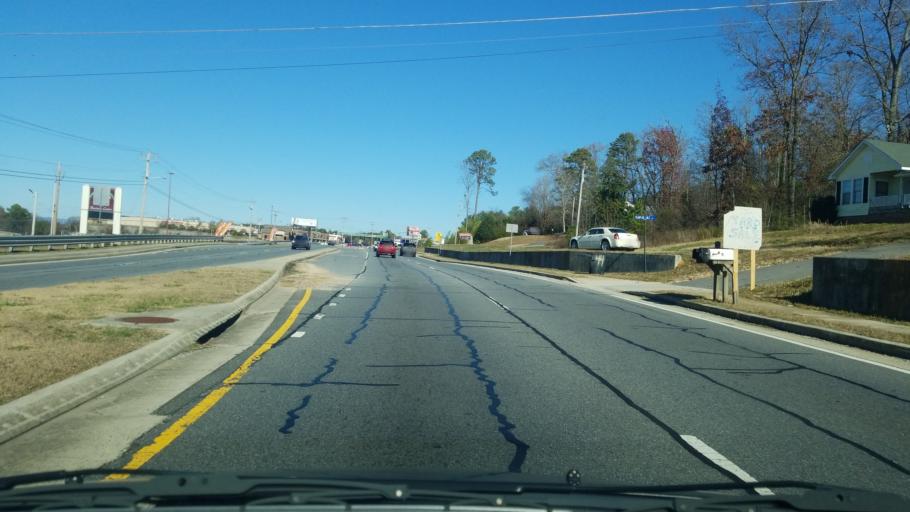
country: US
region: Georgia
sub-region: Catoosa County
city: Indian Springs
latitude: 34.9616
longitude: -85.1950
